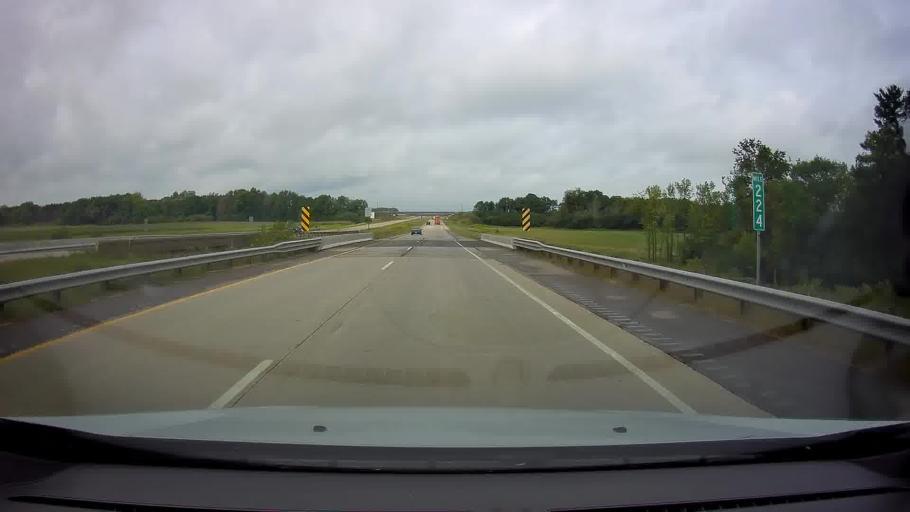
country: US
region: Wisconsin
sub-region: Shawano County
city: Shawano
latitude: 44.7653
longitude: -88.6306
